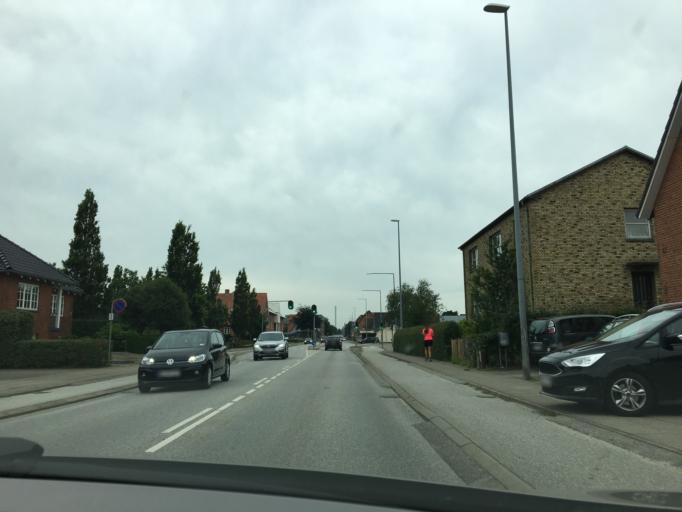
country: DK
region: Central Jutland
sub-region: Herning Kommune
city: Herning
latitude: 56.1418
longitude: 8.9920
